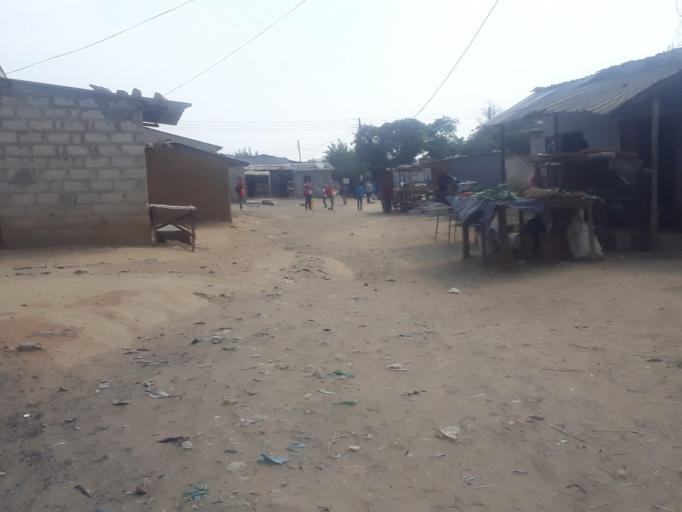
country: ZM
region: Lusaka
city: Lusaka
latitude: -15.3590
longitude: 28.3080
